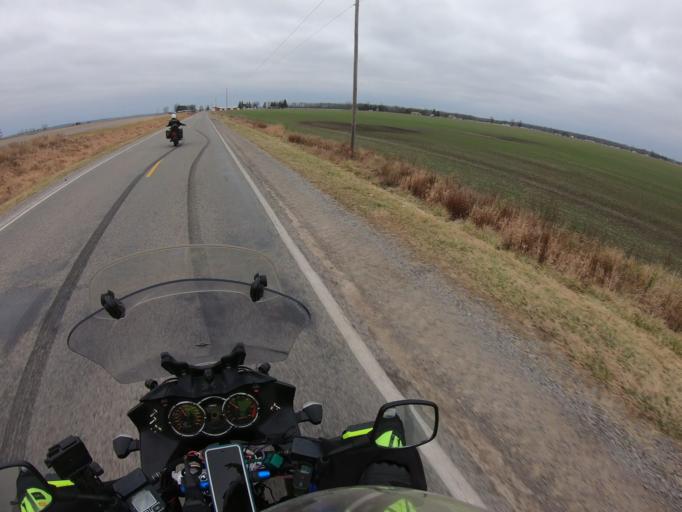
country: US
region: Michigan
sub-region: Saginaw County
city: Burt
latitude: 43.2577
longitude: -83.9717
